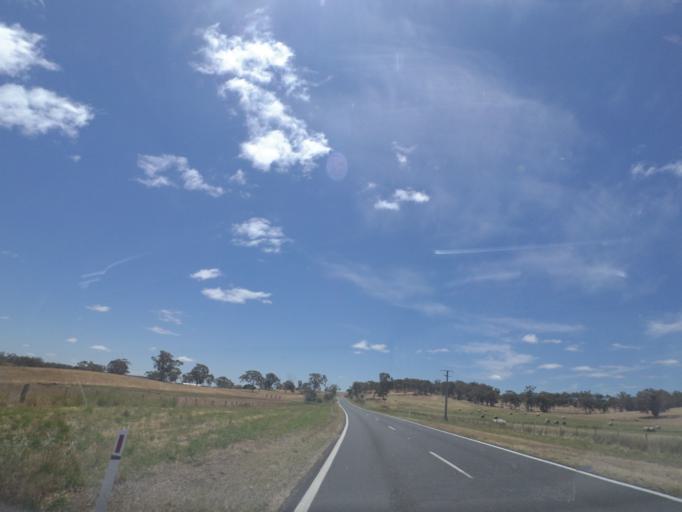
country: AU
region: Victoria
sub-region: Mount Alexander
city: Castlemaine
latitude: -37.2187
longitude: 144.1408
